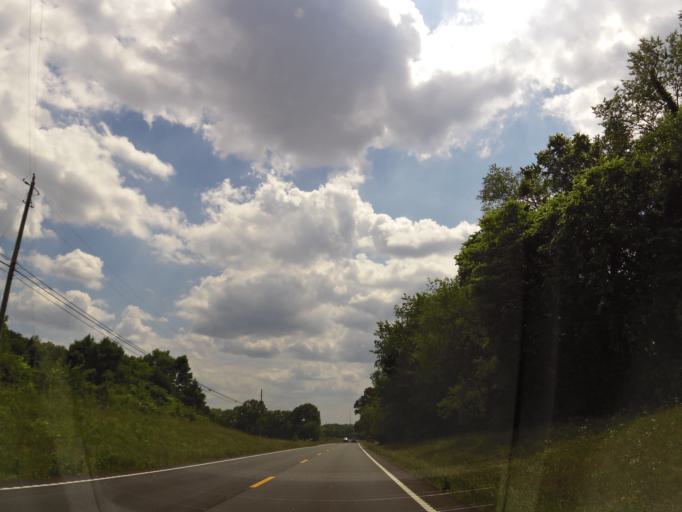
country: US
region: Tennessee
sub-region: Sequatchie County
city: Dunlap
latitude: 35.4690
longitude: -85.3211
